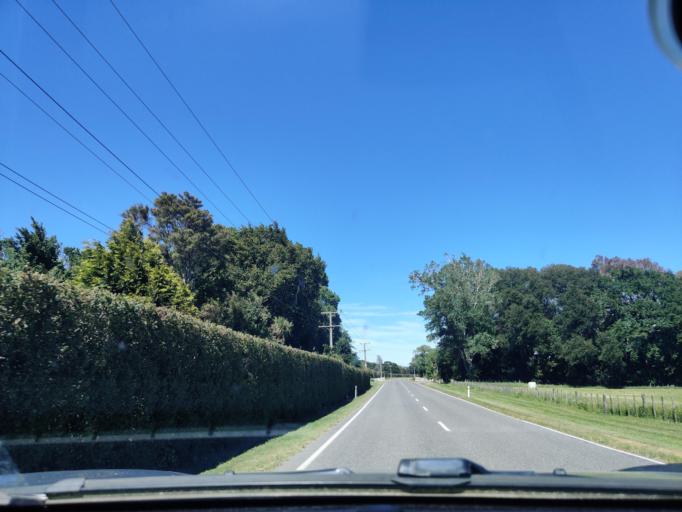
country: NZ
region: Wellington
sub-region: Upper Hutt City
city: Upper Hutt
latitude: -41.3171
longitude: 175.2578
